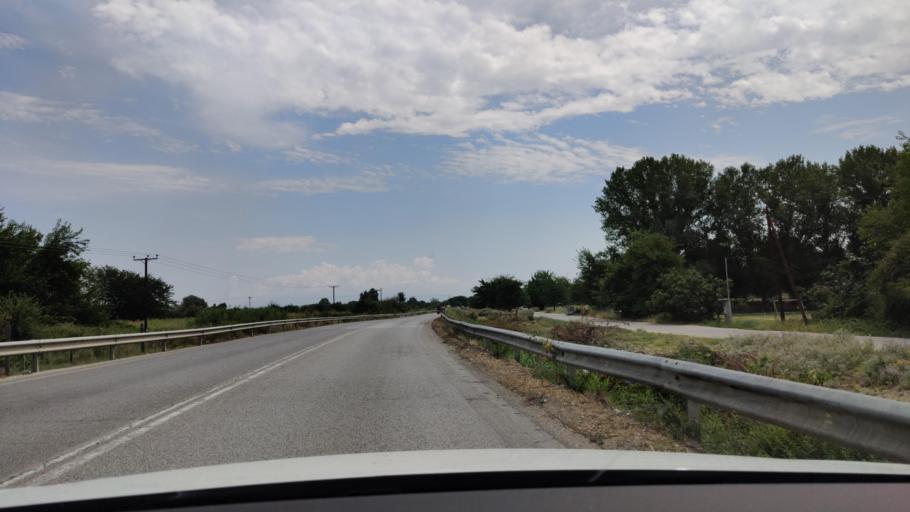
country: GR
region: Central Macedonia
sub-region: Nomos Serron
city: Serres
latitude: 41.0750
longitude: 23.5452
